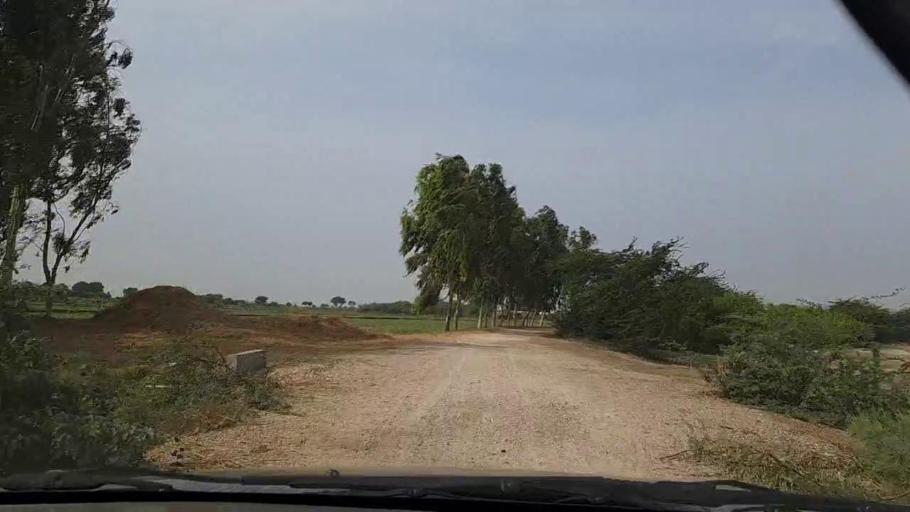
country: PK
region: Sindh
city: Thatta
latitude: 24.5773
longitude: 67.8508
